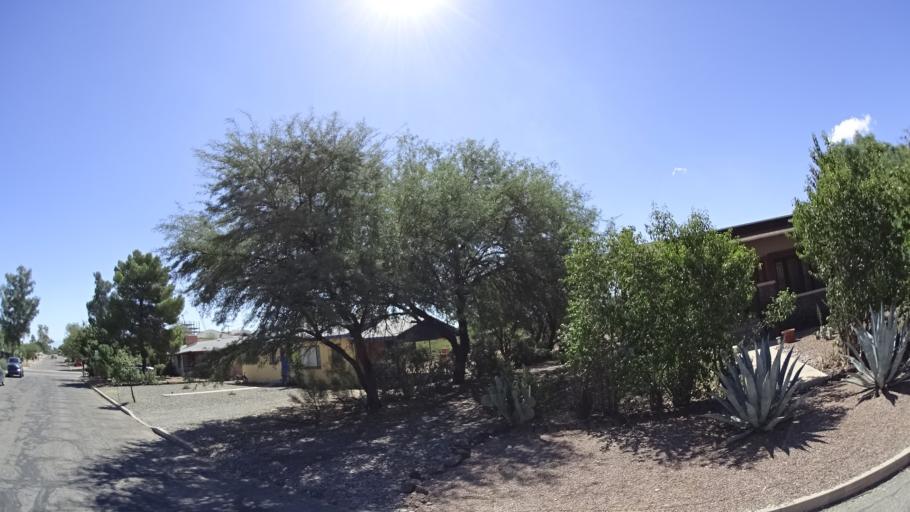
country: US
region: Arizona
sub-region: Pima County
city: Tucson
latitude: 32.2437
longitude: -110.9533
